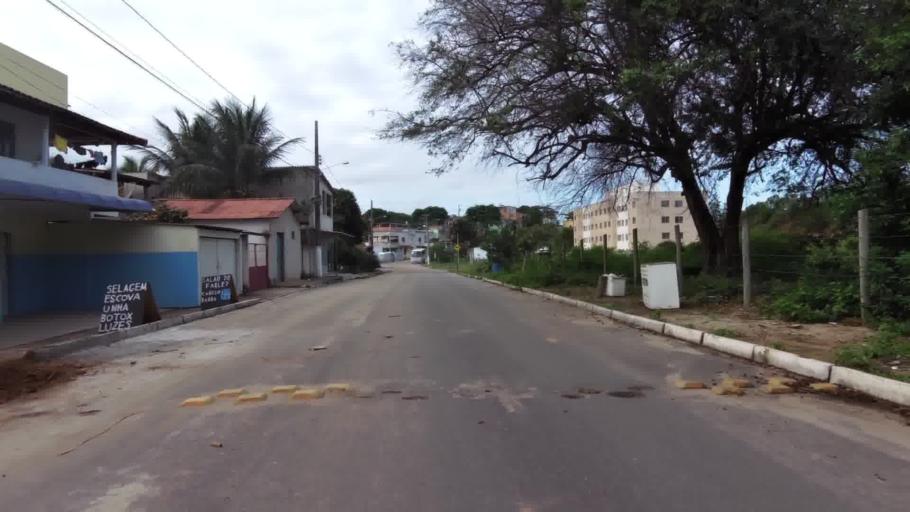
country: BR
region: Espirito Santo
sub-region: Piuma
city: Piuma
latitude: -20.7947
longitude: -40.6393
